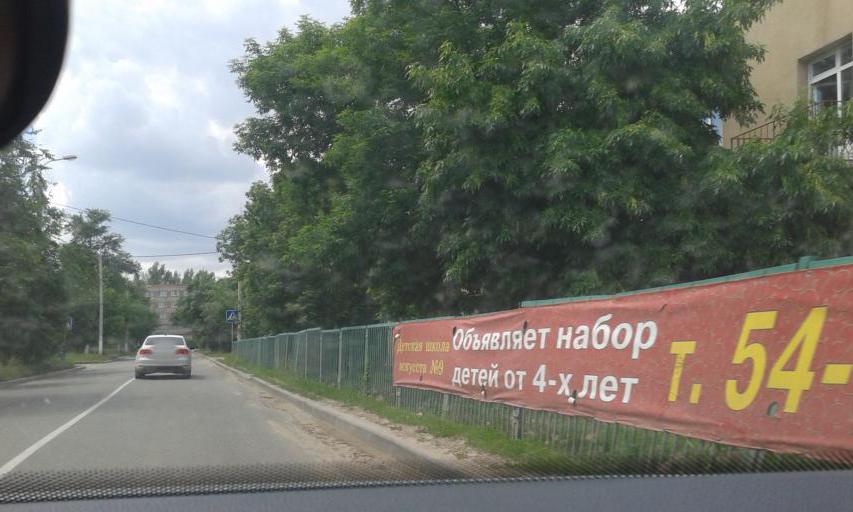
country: RU
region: Volgograd
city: Gorodishche
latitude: 48.7721
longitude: 44.4806
